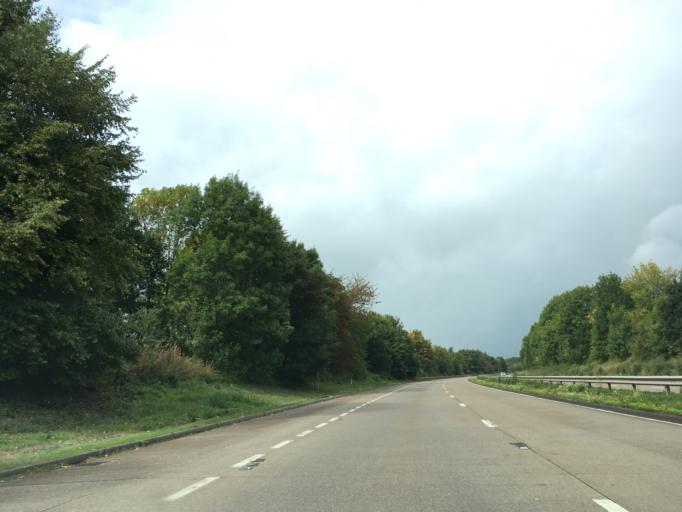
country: GB
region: Wales
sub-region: Monmouthshire
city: Abergavenny
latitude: 51.7867
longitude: -2.9842
